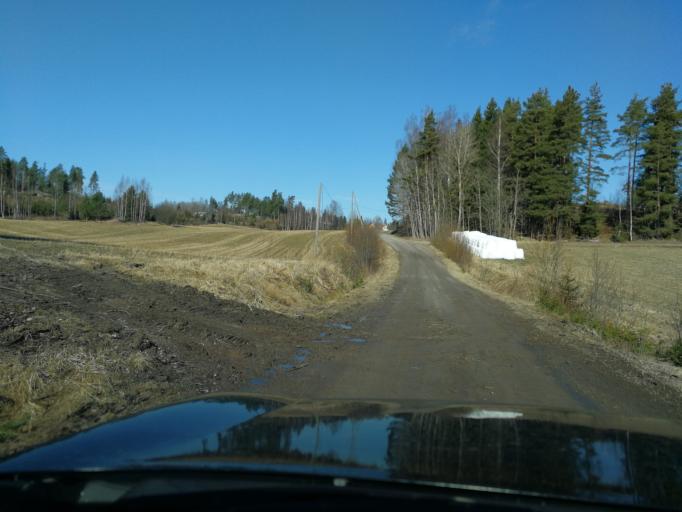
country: FI
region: Uusimaa
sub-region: Helsinki
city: Karjalohja
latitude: 60.2117
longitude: 23.7017
